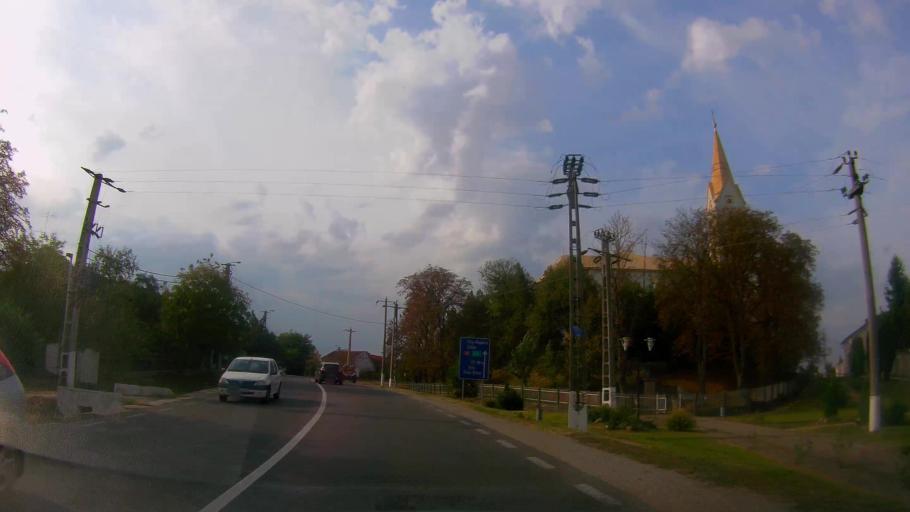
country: RO
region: Satu Mare
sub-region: Oras Ardud
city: Ardud
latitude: 47.6386
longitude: 22.8874
